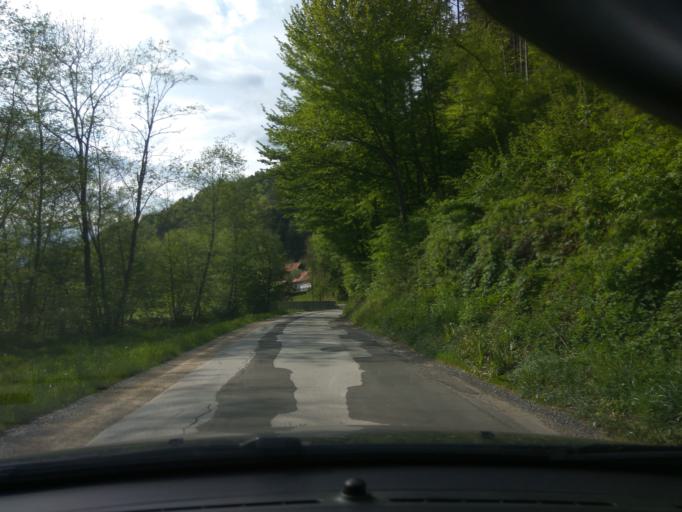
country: AT
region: Styria
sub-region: Politischer Bezirk Voitsberg
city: Voitsberg
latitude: 47.0265
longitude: 15.1491
